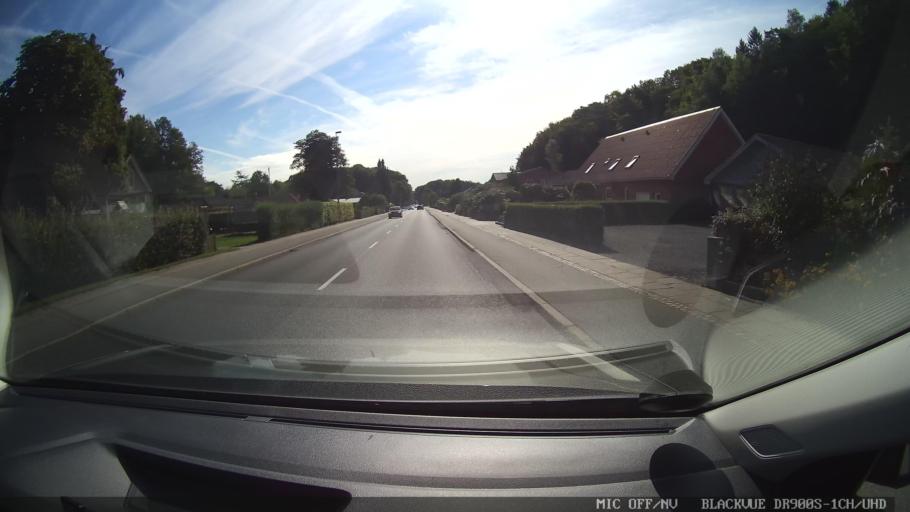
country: DK
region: North Denmark
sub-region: Mariagerfjord Kommune
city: Hadsund
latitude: 56.7202
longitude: 10.1041
